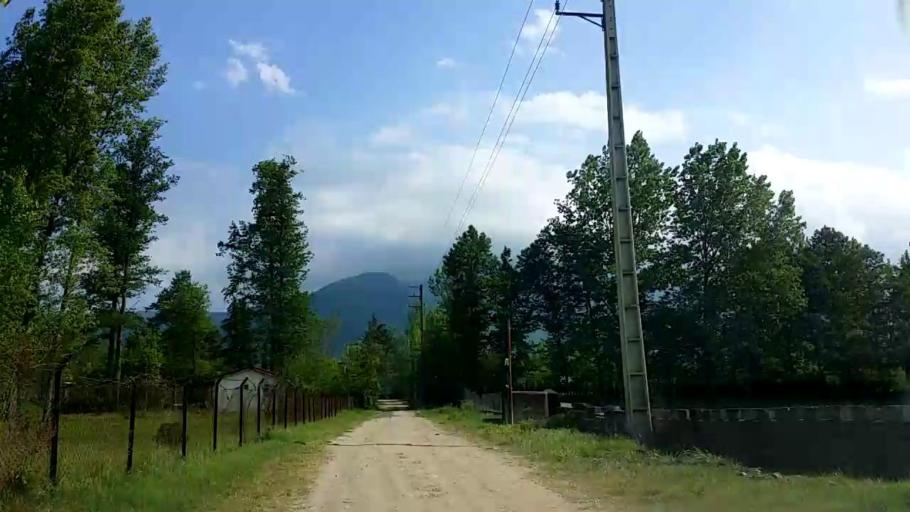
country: IR
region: Mazandaran
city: `Abbasabad
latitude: 36.5266
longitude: 51.1828
